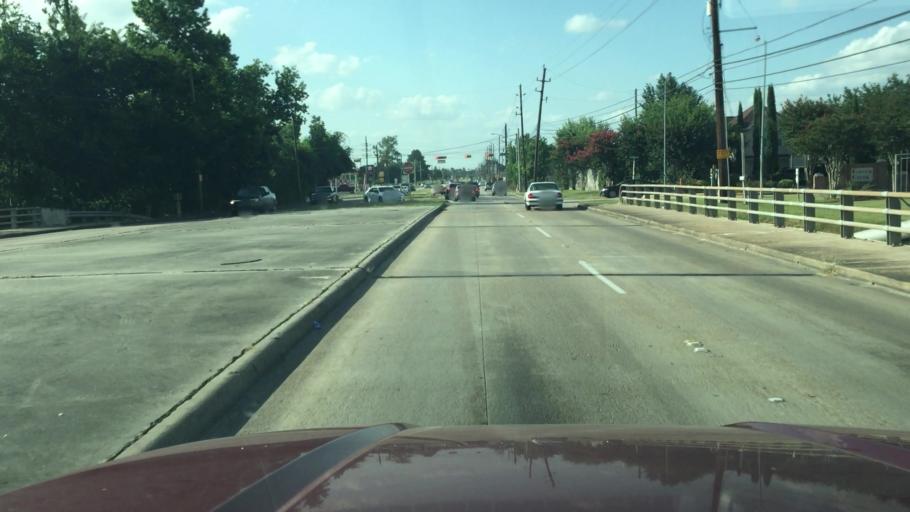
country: US
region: Texas
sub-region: Harris County
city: Hudson
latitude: 29.9486
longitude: -95.4981
